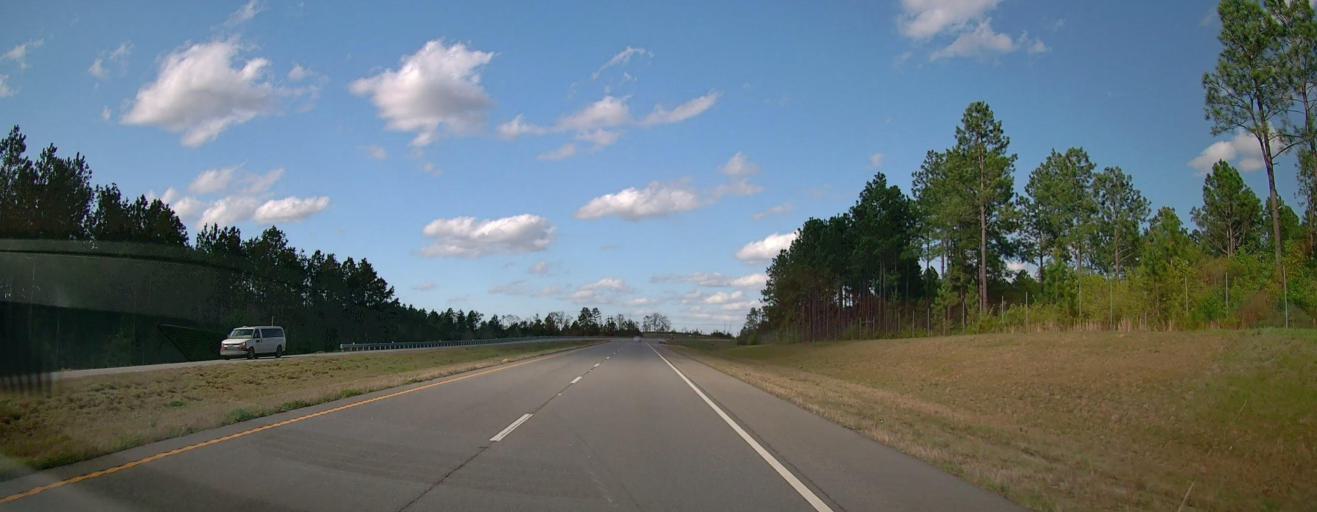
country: US
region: Georgia
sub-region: Baldwin County
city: Hardwick
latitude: 32.9929
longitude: -83.2044
